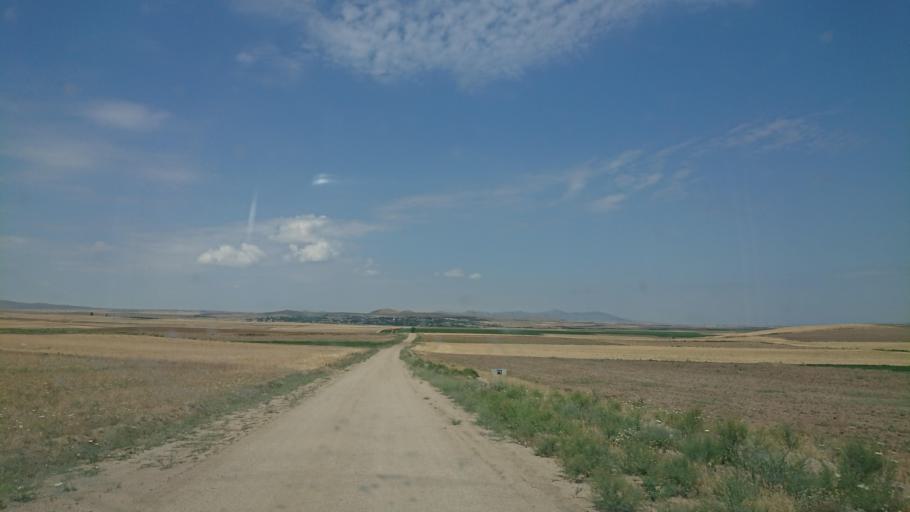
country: TR
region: Aksaray
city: Agacoren
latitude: 38.9553
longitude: 33.9257
